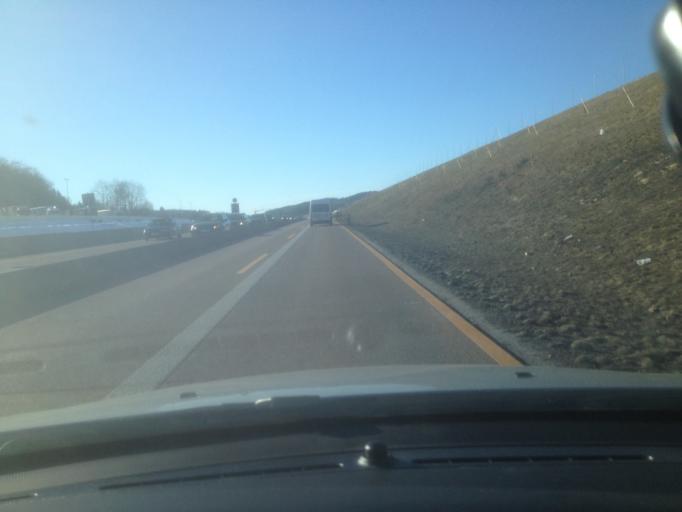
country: DE
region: Bavaria
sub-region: Swabia
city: Gablingen
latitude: 48.4196
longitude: 10.8119
